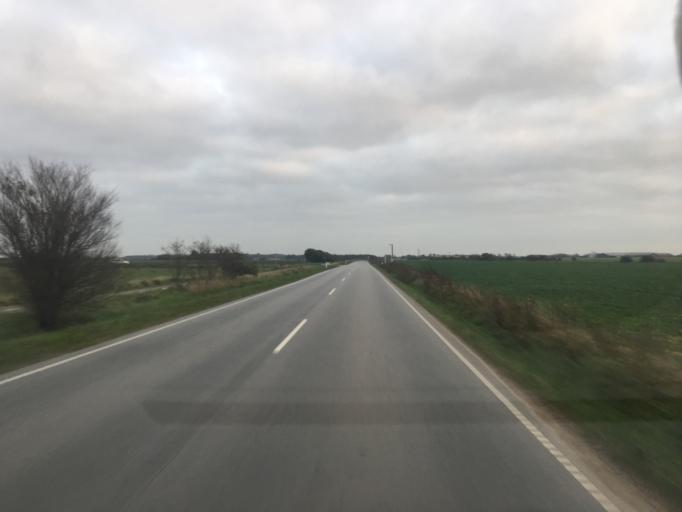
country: DE
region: Schleswig-Holstein
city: Aventoft
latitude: 54.9604
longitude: 8.7609
